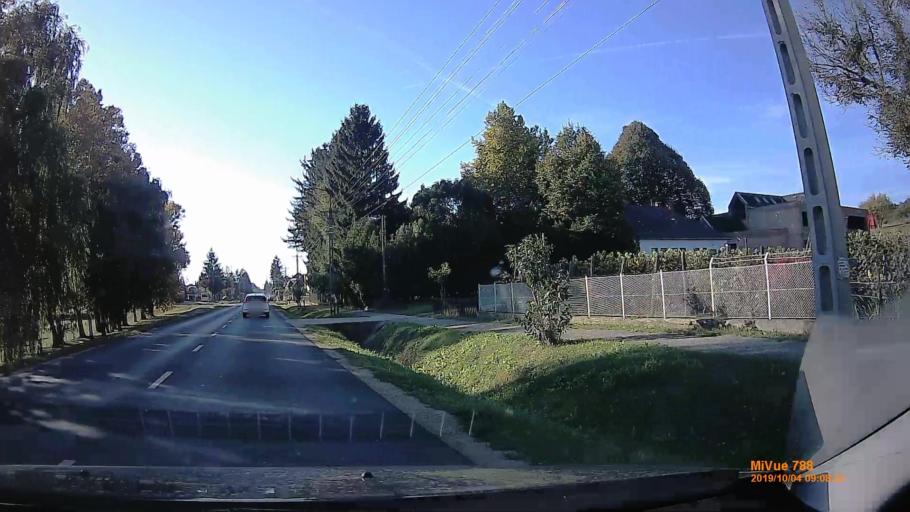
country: HU
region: Somogy
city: Karad
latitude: 46.6712
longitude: 17.7773
